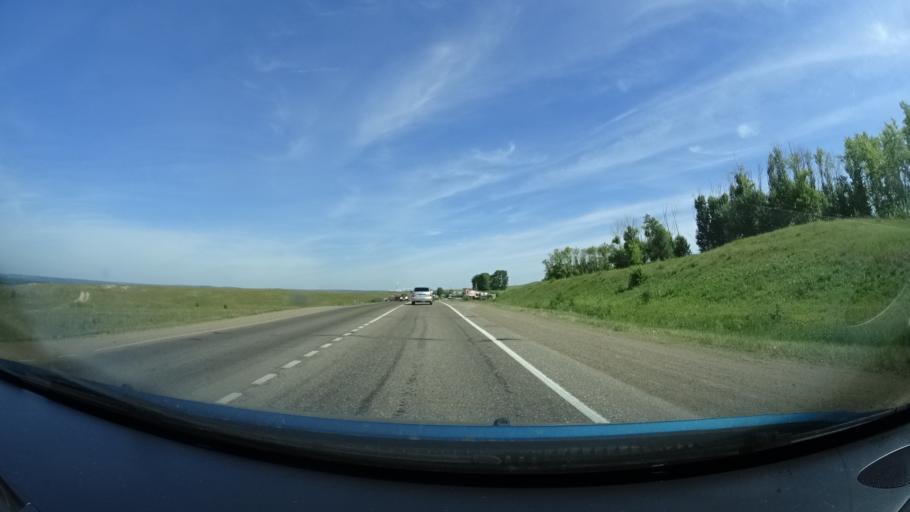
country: RU
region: Bashkortostan
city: Blagoveshchensk
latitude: 55.1695
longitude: 55.8535
